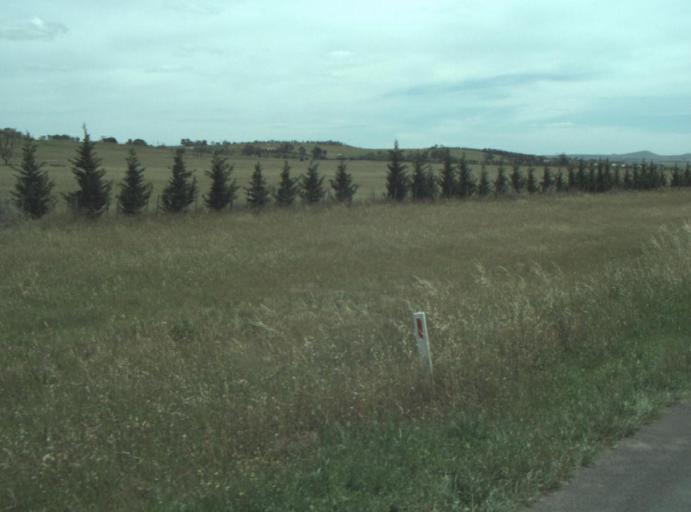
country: AU
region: Victoria
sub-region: Greater Geelong
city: Lara
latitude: -38.0207
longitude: 144.3526
